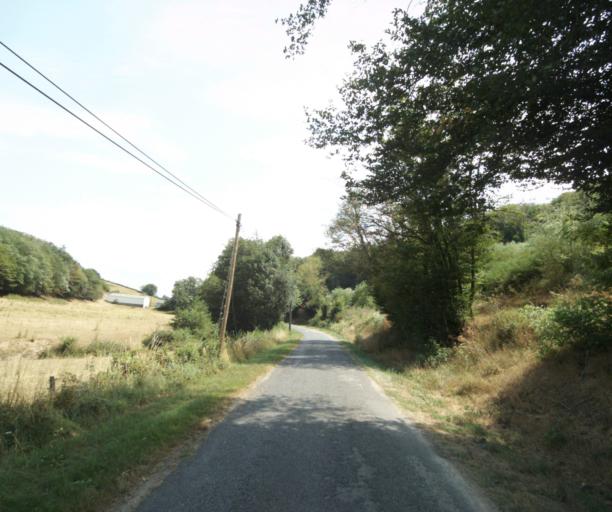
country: FR
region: Bourgogne
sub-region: Departement de Saone-et-Loire
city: Gueugnon
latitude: 46.6171
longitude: 4.0288
